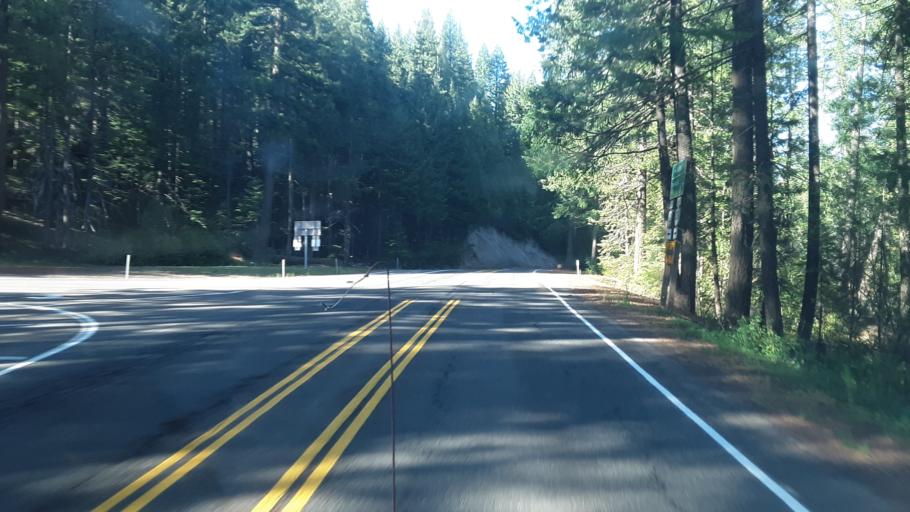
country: US
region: Oregon
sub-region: Jackson County
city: Shady Cove
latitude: 42.9215
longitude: -122.4292
